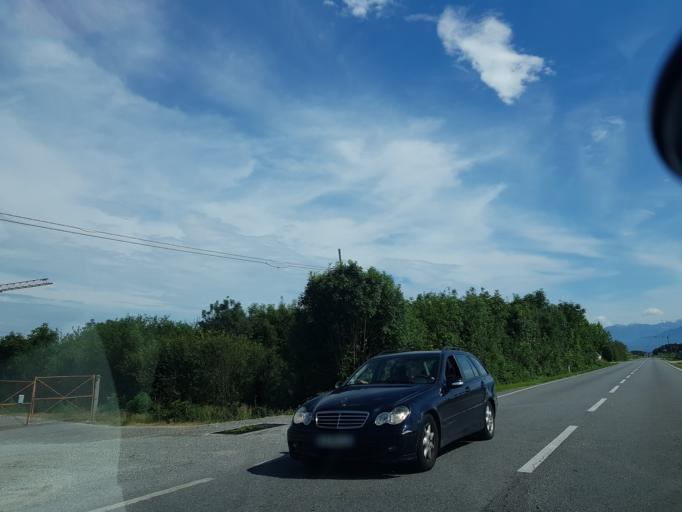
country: IT
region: Piedmont
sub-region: Provincia di Cuneo
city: Busca
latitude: 44.4913
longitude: 7.4977
